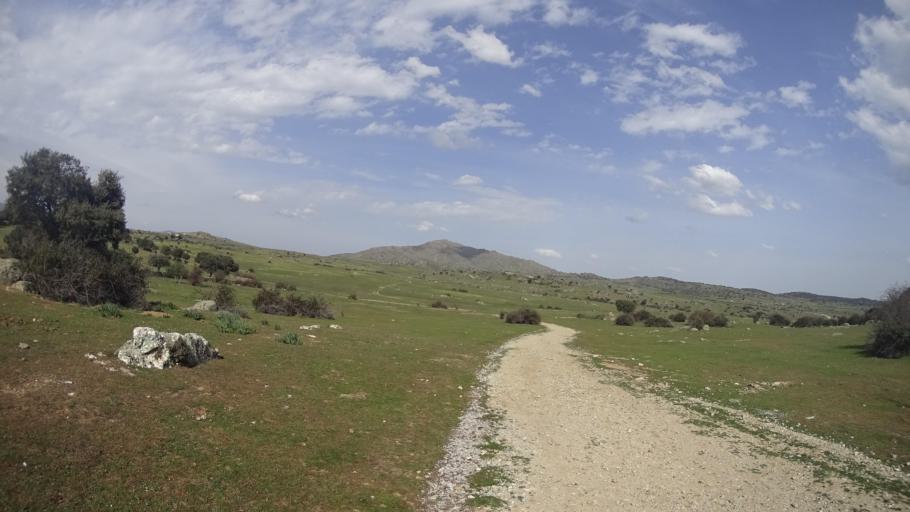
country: ES
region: Madrid
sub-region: Provincia de Madrid
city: Colmenar Viejo
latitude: 40.7031
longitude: -3.7613
